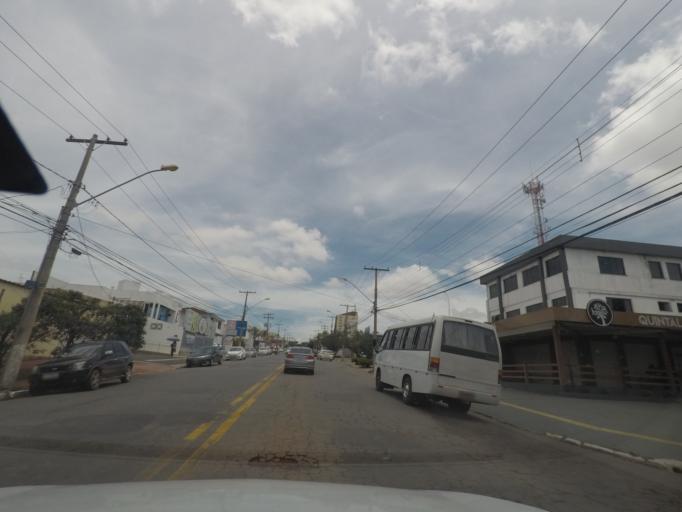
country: BR
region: Goias
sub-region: Goiania
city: Goiania
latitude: -16.6869
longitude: -49.2486
